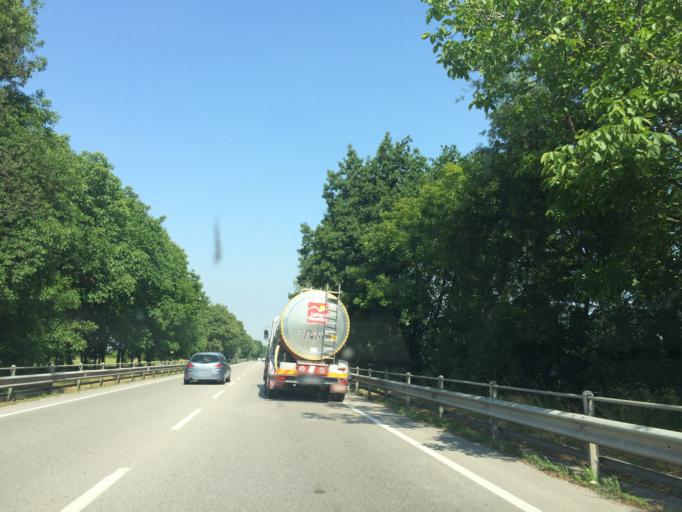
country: IT
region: Veneto
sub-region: Provincia di Padova
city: Cittadella
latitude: 45.6312
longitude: 11.7838
